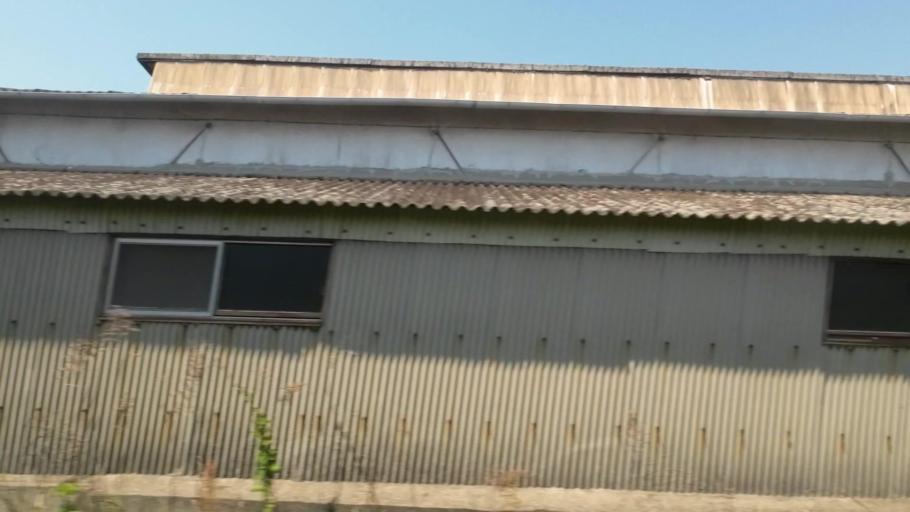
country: JP
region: Ehime
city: Hojo
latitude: 33.9662
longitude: 132.7739
